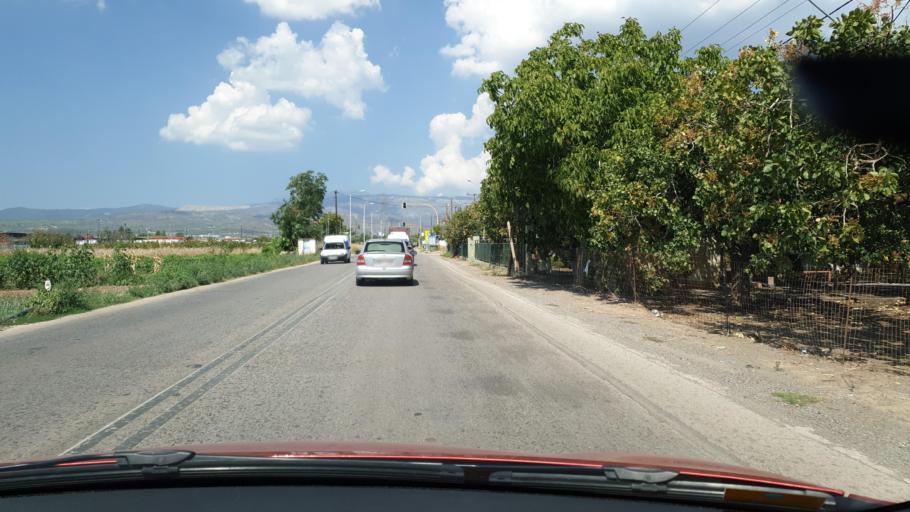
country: GR
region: Central Greece
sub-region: Nomos Evvoias
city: Kastella
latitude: 38.5557
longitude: 23.6323
